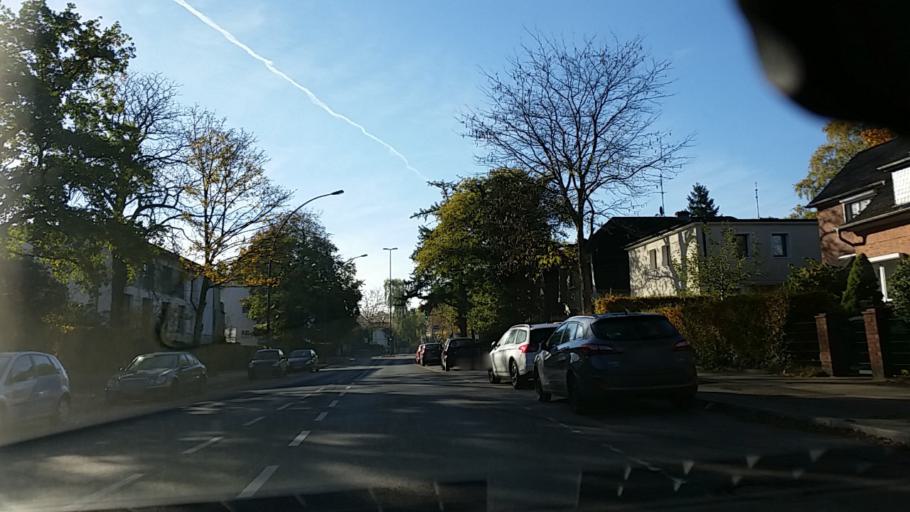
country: DE
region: Schleswig-Holstein
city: Halstenbek
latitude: 53.5678
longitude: 9.8281
